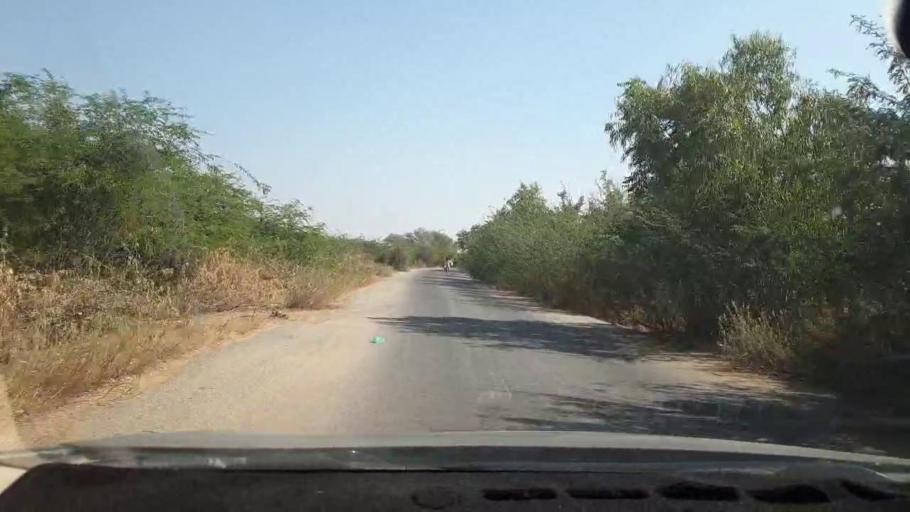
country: PK
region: Sindh
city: Malir Cantonment
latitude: 25.1416
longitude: 67.1988
